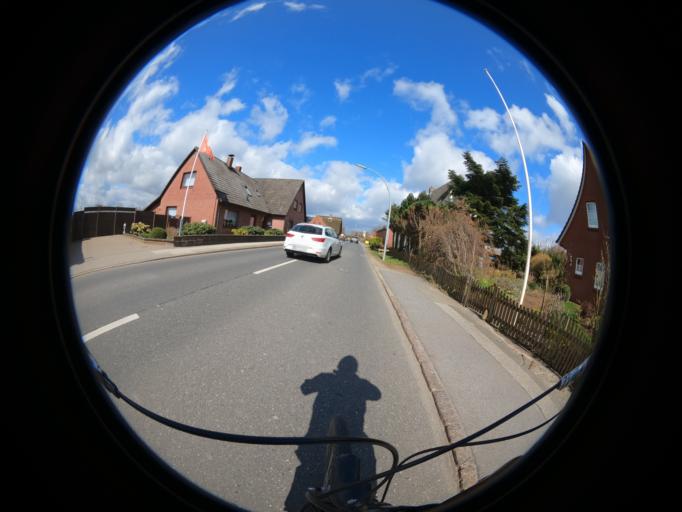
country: DE
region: Lower Saxony
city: Neu Wulmstorf
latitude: 53.5135
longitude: 9.7921
